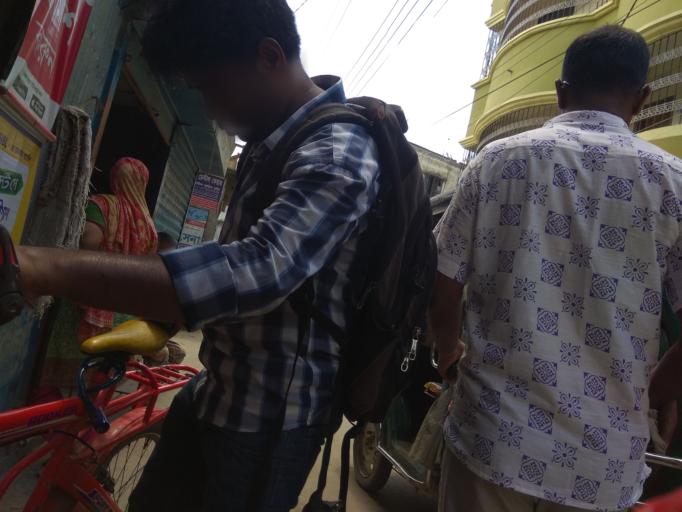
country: BD
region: Dhaka
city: Tungi
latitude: 23.8239
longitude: 90.3886
